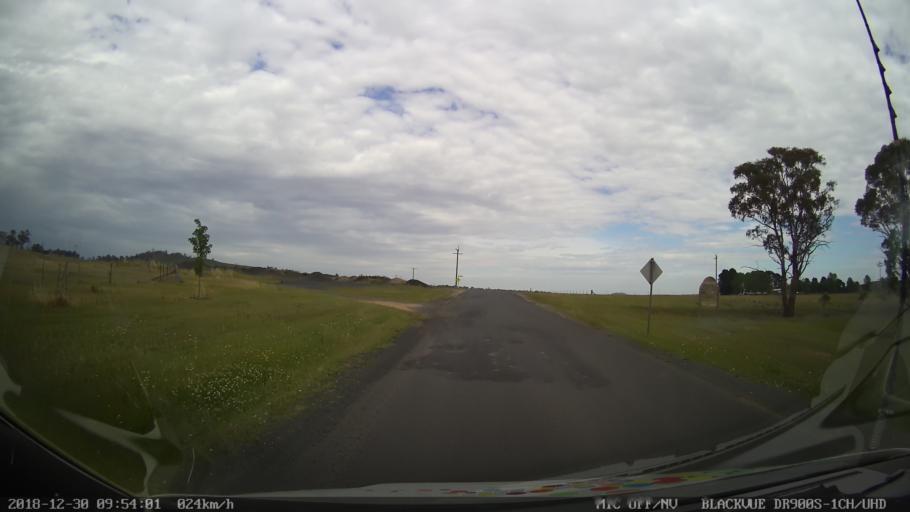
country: AU
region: New South Wales
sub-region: Cooma-Monaro
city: Cooma
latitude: -36.5184
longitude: 149.2807
